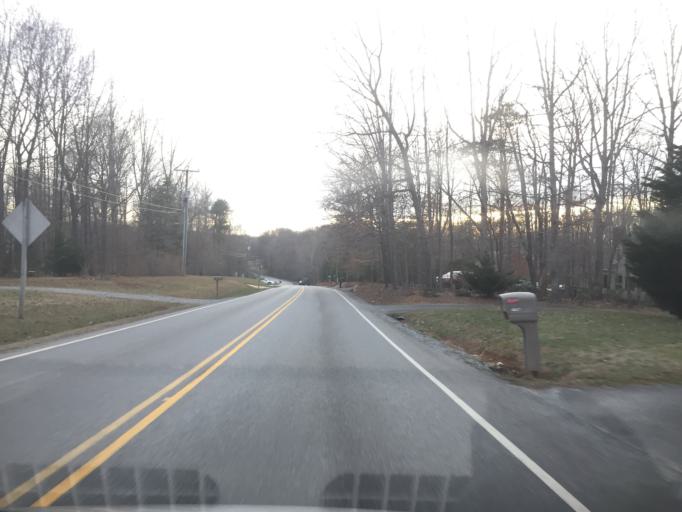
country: US
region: Virginia
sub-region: Bedford County
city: Forest
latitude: 37.3257
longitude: -79.3037
